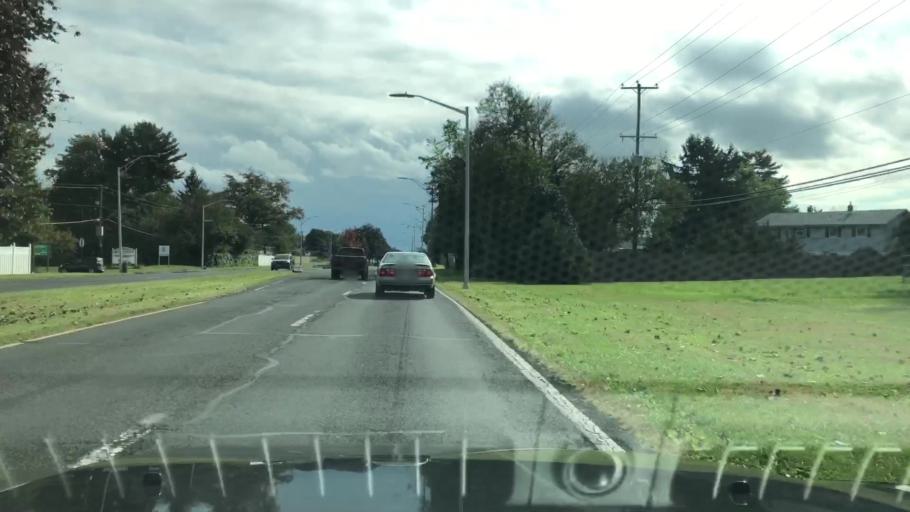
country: US
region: Pennsylvania
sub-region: Bucks County
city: Levittown
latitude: 40.1511
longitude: -74.8255
